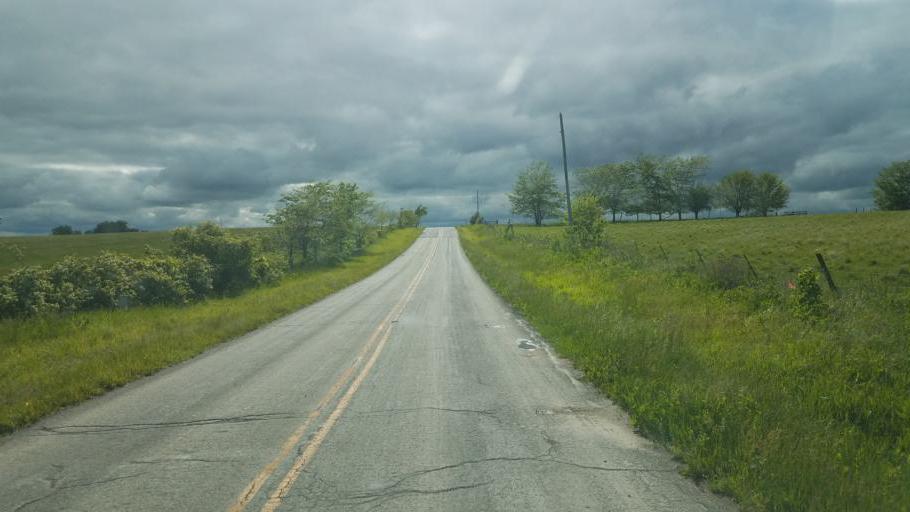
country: US
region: Missouri
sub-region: Mercer County
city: Princeton
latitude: 40.2493
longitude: -93.6785
